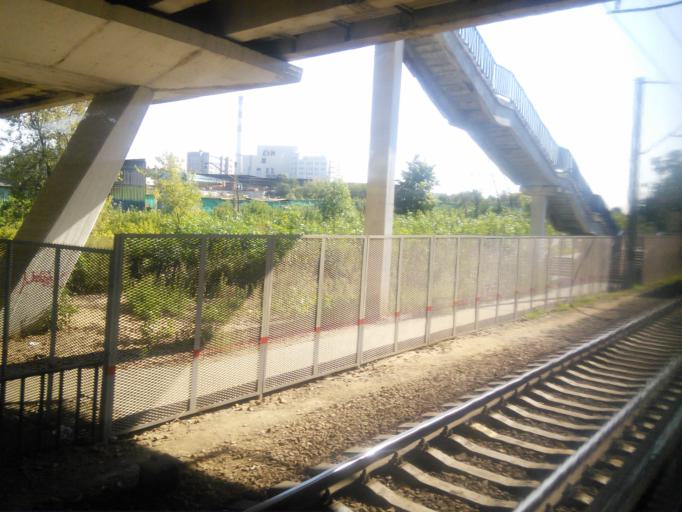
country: RU
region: Moskovskaya
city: Biryulevo Zapadnoye
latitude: 55.6043
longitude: 37.6333
